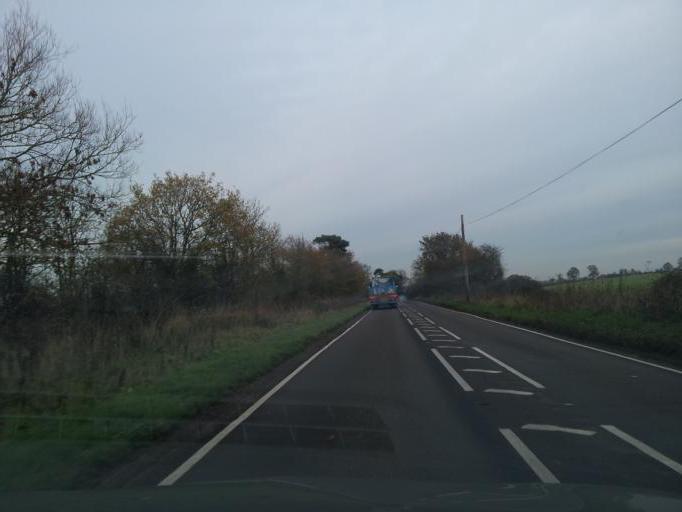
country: GB
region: England
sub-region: Buckinghamshire
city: Stewkley
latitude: 51.8743
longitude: -0.7517
